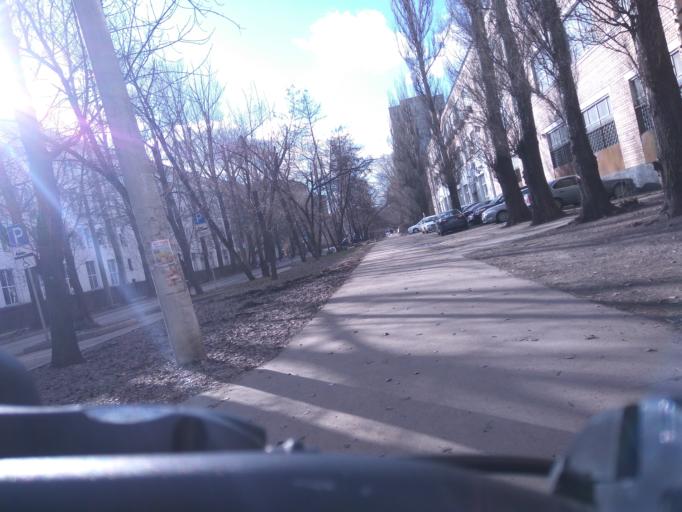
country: RU
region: Moscow
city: Sokol'niki
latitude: 55.8041
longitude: 37.6502
